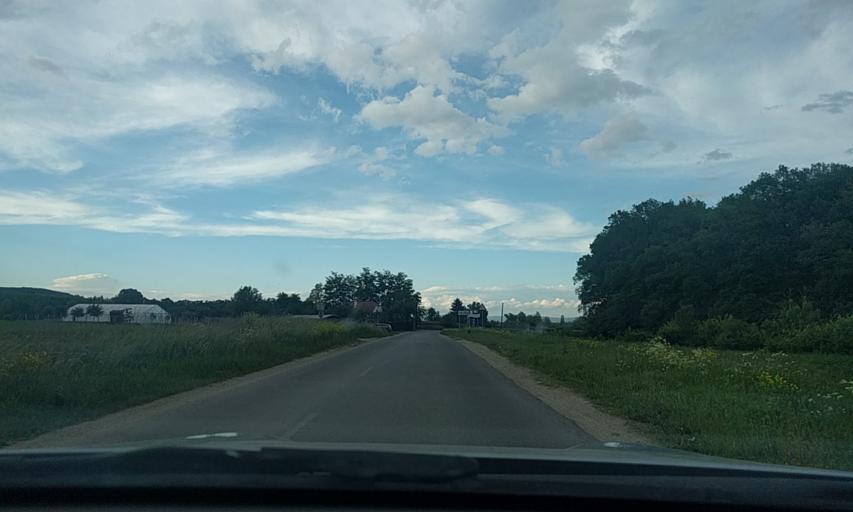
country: RO
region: Brasov
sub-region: Comuna Harman
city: Harman
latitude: 45.7481
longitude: 25.7047
